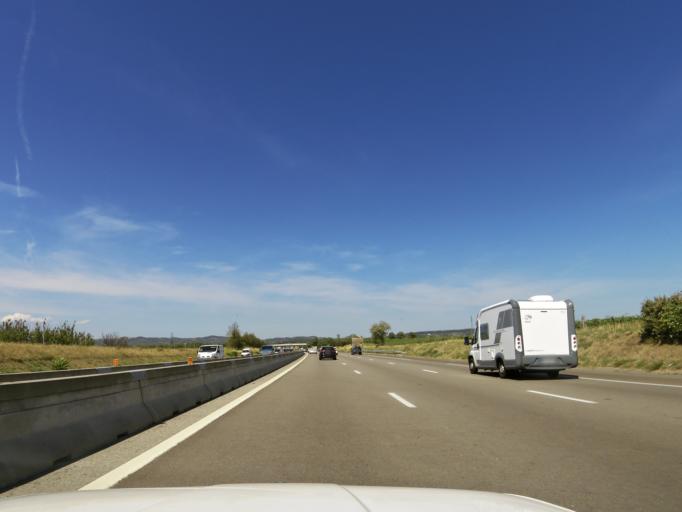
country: FR
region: Rhone-Alpes
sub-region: Departement de la Drome
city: Mercurol
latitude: 45.0438
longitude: 4.8783
